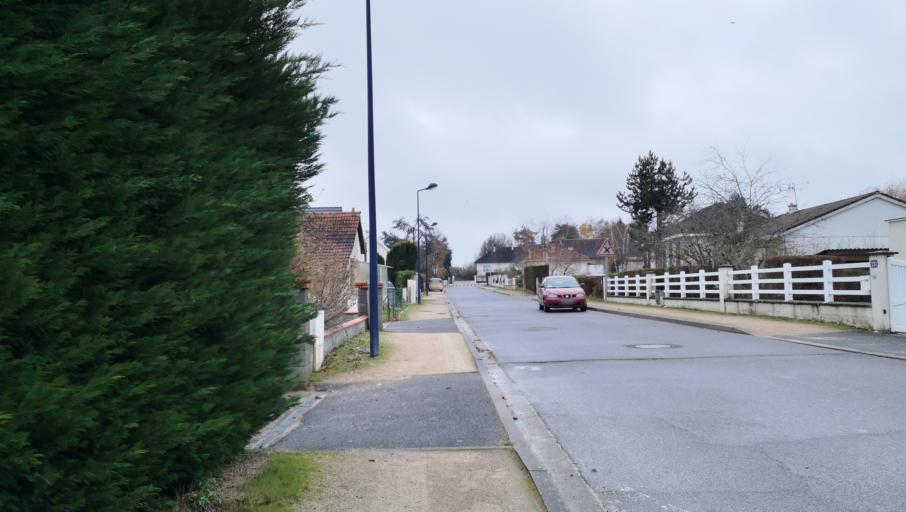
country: FR
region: Centre
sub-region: Departement du Loiret
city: Semoy
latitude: 47.9322
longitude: 1.9539
